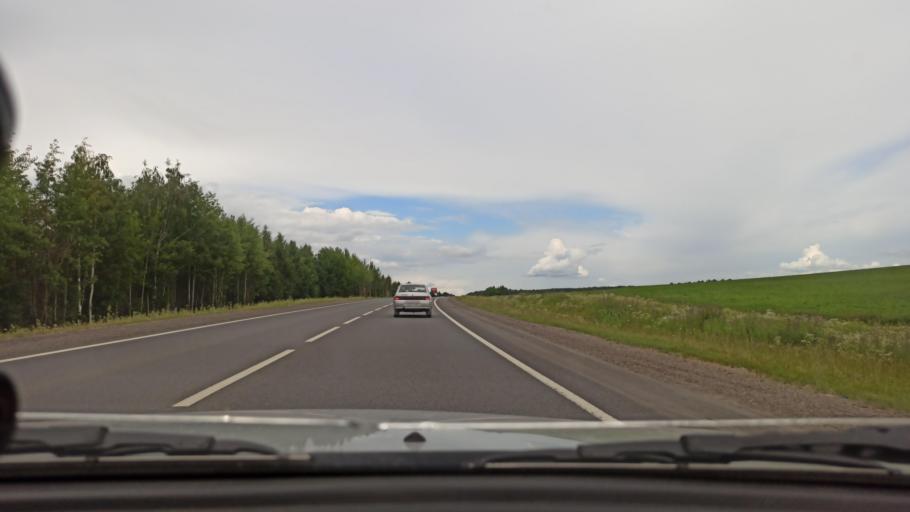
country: RU
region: Vologda
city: Molochnoye
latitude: 59.2921
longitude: 39.6892
